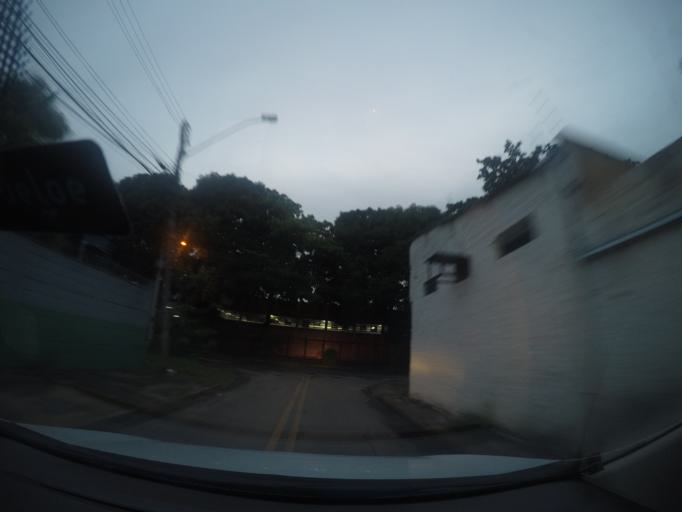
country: BR
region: Goias
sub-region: Goiania
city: Goiania
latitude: -16.6416
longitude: -49.2440
